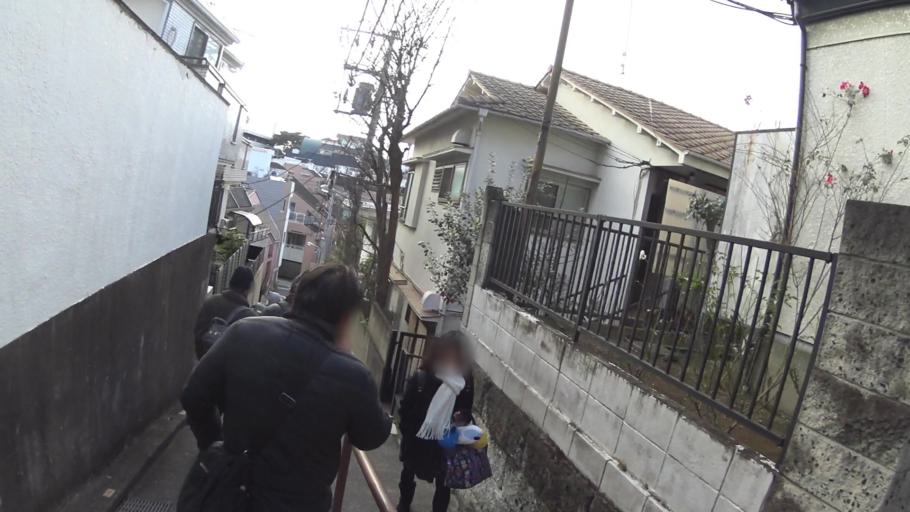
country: JP
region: Tokyo
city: Tokyo
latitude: 35.6725
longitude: 139.6832
